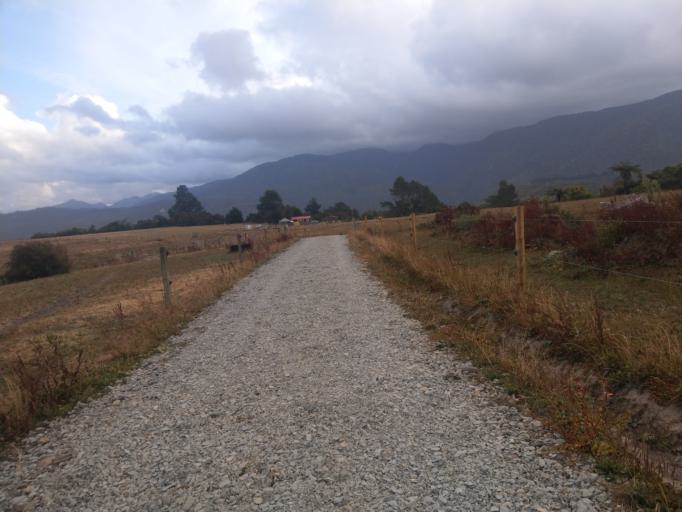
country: NZ
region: Tasman
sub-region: Tasman District
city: Takaka
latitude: -40.7910
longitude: 172.7442
